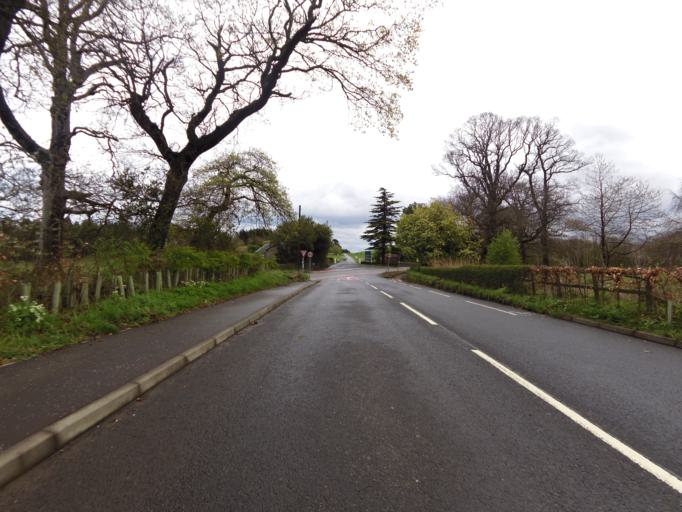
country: GB
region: Scotland
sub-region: Edinburgh
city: Queensferry
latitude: 55.9844
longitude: -3.3600
